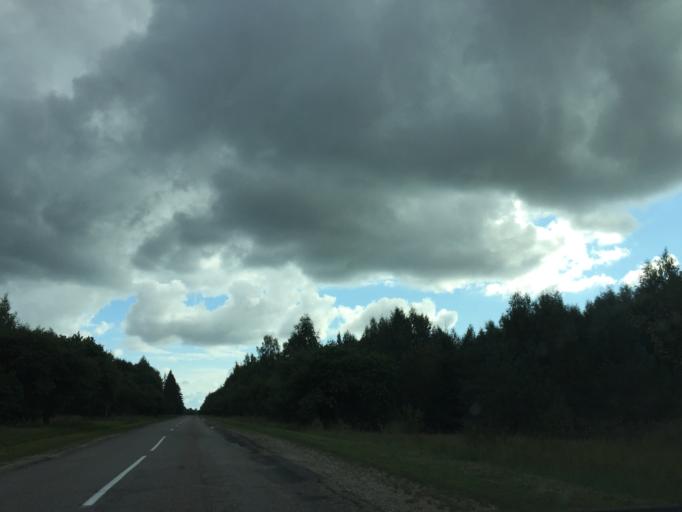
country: LV
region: Limbazu Rajons
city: Limbazi
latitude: 57.3640
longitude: 24.6712
